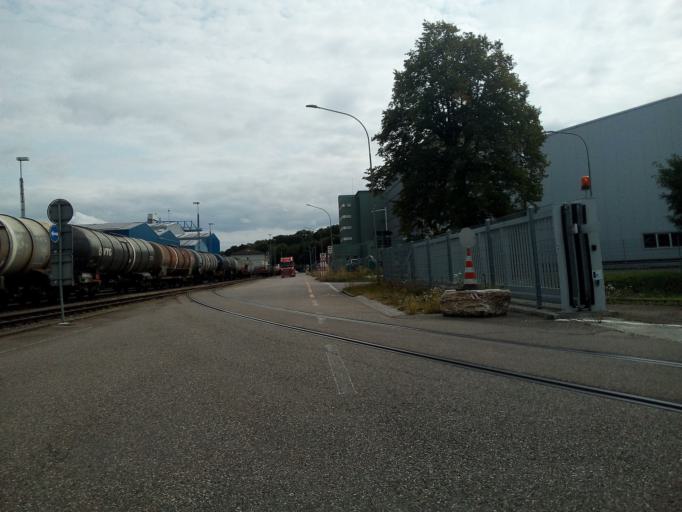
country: CH
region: Basel-Landschaft
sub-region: Bezirk Arlesheim
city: Birsfelden
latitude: 47.5538
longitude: 7.6402
